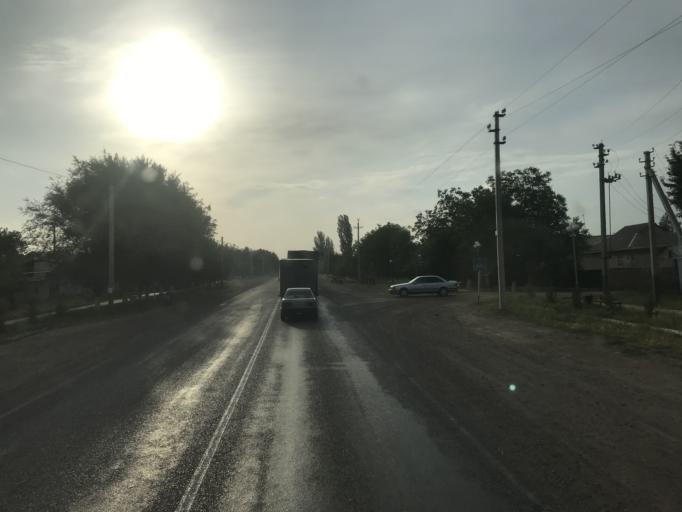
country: UZ
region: Toshkent
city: Salor
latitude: 41.4937
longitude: 69.3136
